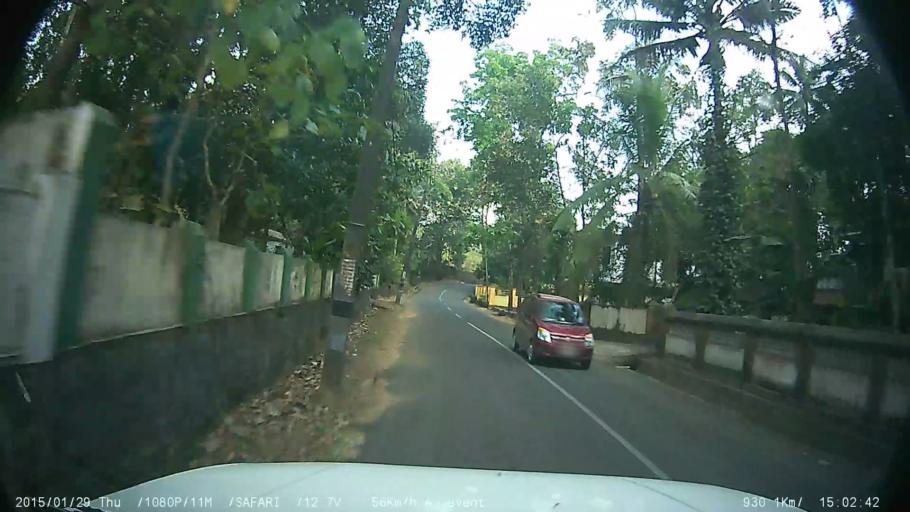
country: IN
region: Kerala
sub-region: Kottayam
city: Palackattumala
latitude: 9.7261
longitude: 76.5776
